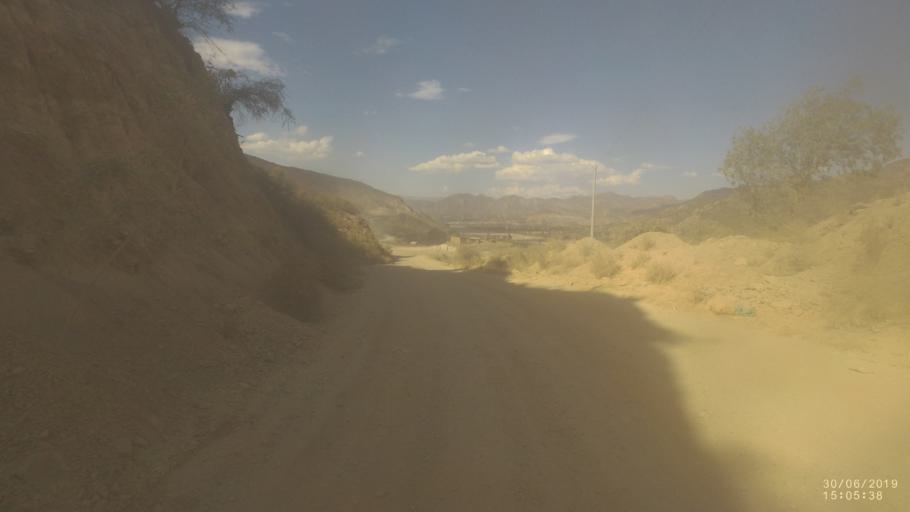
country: BO
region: Cochabamba
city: Irpa Irpa
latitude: -17.7327
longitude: -66.3160
